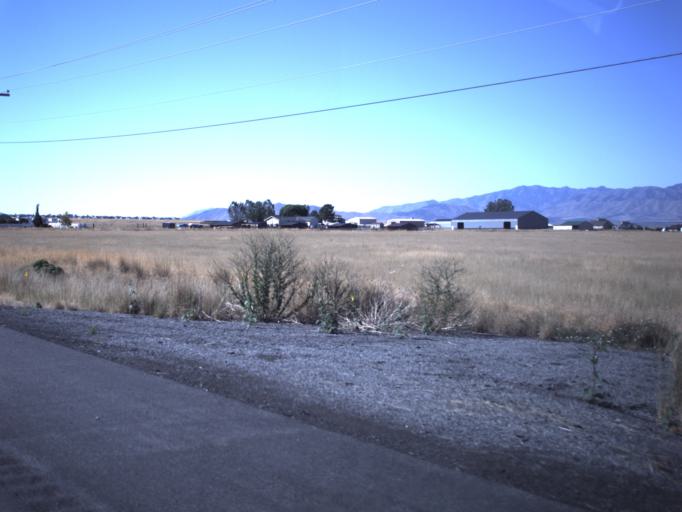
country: US
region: Utah
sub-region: Tooele County
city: Erda
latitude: 40.5974
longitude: -112.2942
